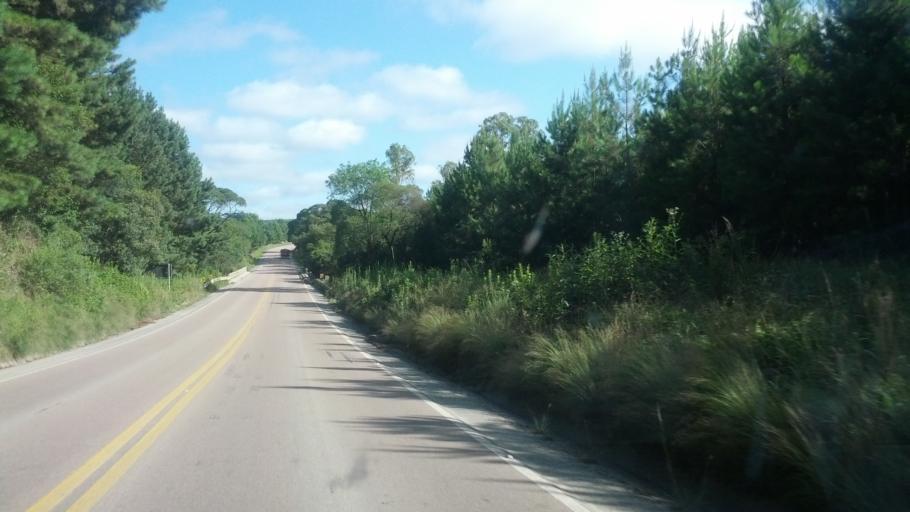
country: BR
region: Santa Catarina
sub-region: Otacilio Costa
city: Otacilio Costa
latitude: -27.4648
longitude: -50.1226
